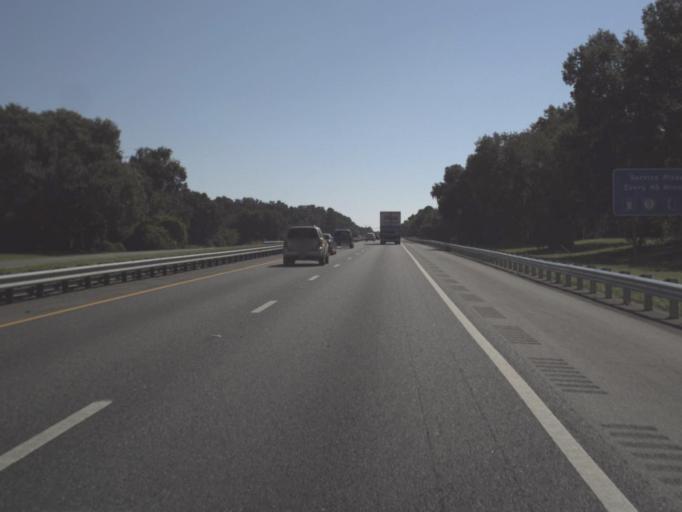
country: US
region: Florida
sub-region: Sumter County
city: Wildwood
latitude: 28.8243
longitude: -82.0253
